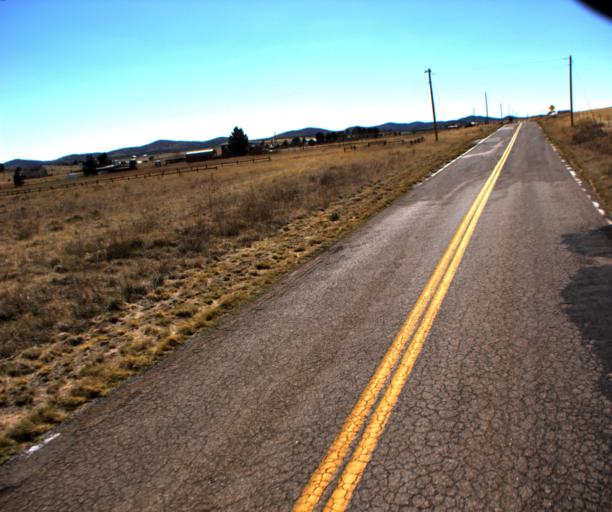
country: US
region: Arizona
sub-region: Cochise County
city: Huachuca City
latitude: 31.6080
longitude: -110.5800
